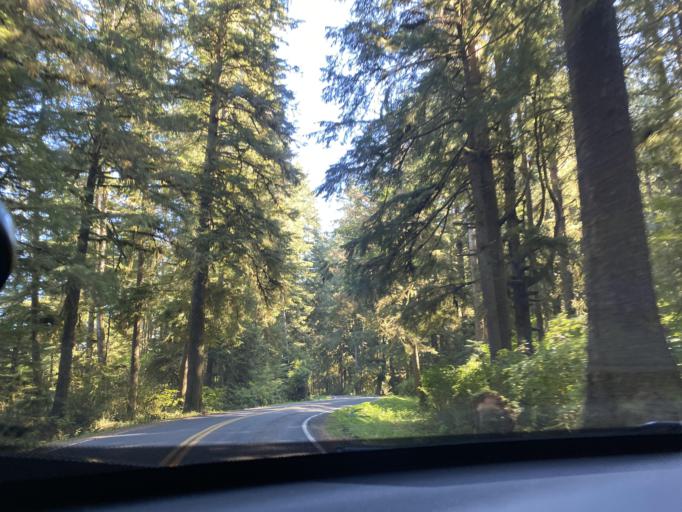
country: US
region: Washington
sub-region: Clallam County
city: Forks
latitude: 47.9196
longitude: -124.6104
